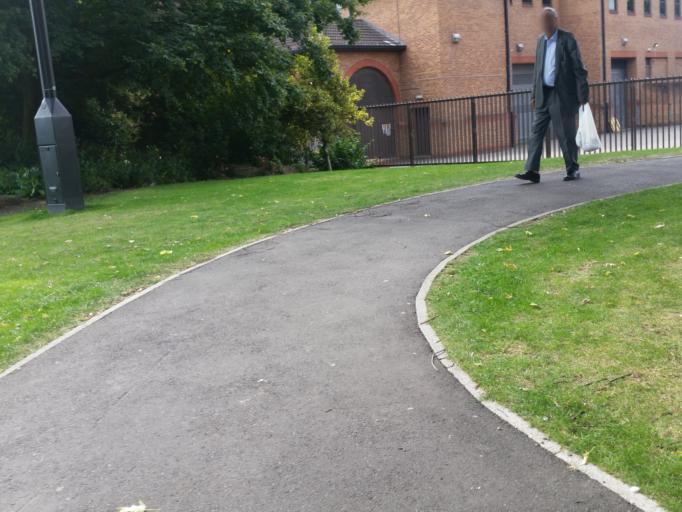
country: GB
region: England
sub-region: Derby
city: Derby
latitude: 52.9230
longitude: -1.4732
